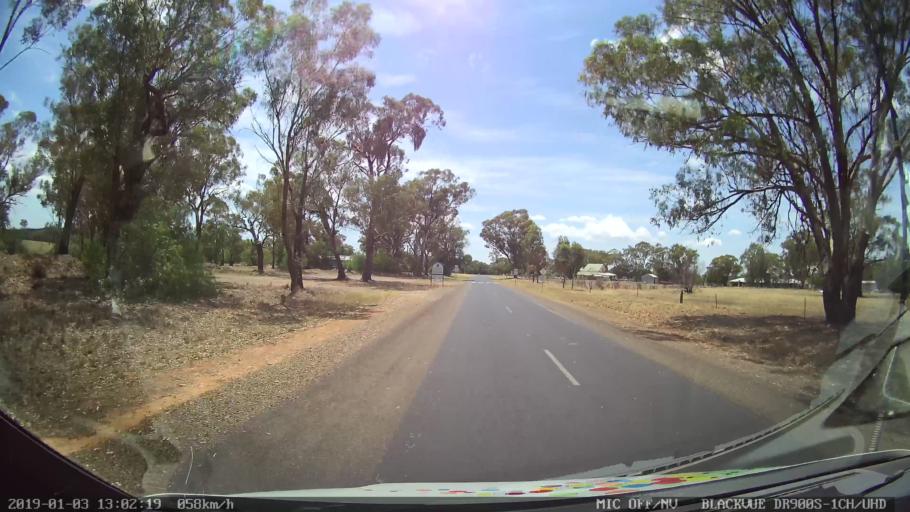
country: AU
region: New South Wales
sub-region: Cabonne
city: Canowindra
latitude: -33.6185
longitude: 148.4279
